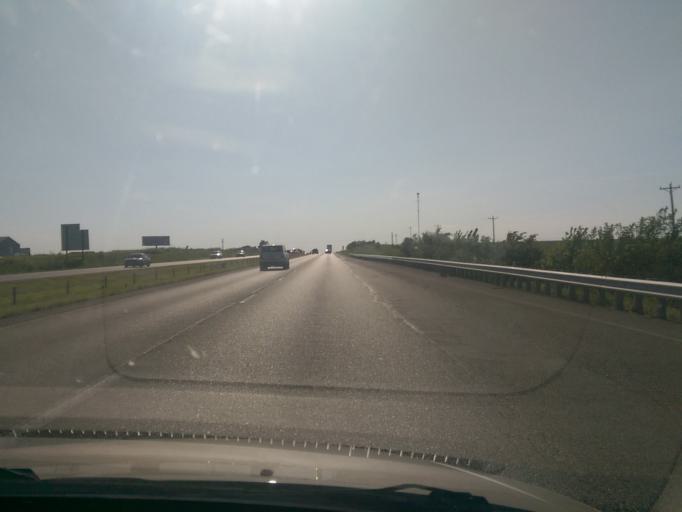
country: US
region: Missouri
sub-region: Lafayette County
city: Odessa
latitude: 39.0059
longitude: -93.8916
